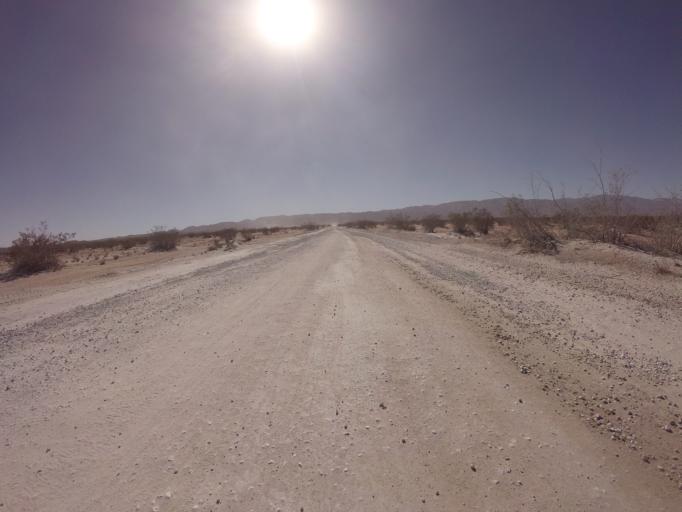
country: US
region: California
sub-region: San Bernardino County
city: Yucca Valley
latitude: 34.3813
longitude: -116.5437
